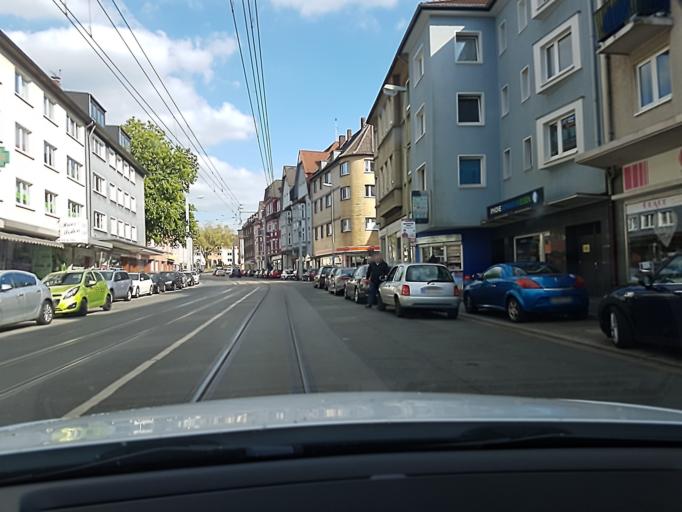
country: DE
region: North Rhine-Westphalia
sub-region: Regierungsbezirk Dusseldorf
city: Essen
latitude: 51.4396
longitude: 7.0238
